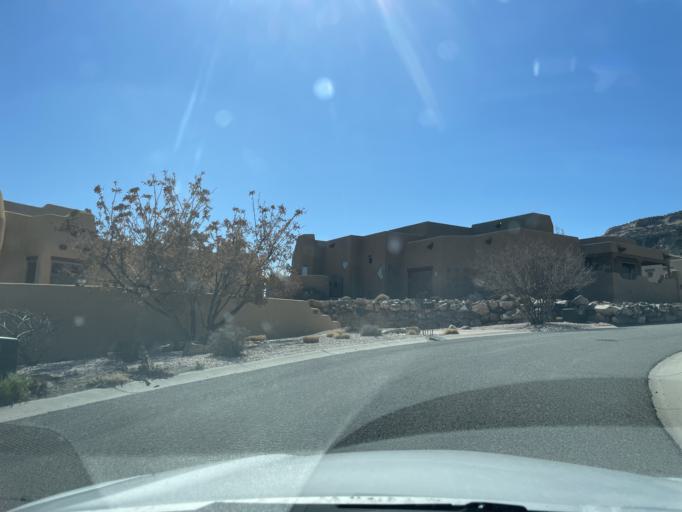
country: US
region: Colorado
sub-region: Mesa County
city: Redlands
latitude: 39.0750
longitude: -108.6706
